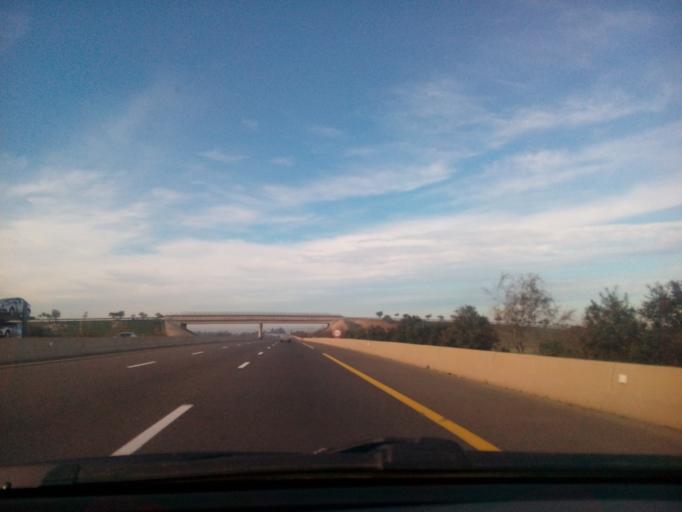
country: DZ
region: Mascara
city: Sig
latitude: 35.6164
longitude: 0.0076
